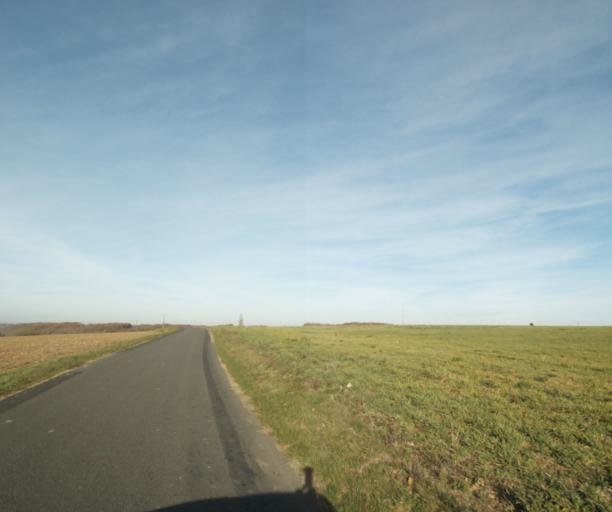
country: FR
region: Poitou-Charentes
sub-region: Departement de la Charente-Maritime
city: Chaniers
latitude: 45.7196
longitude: -0.5288
